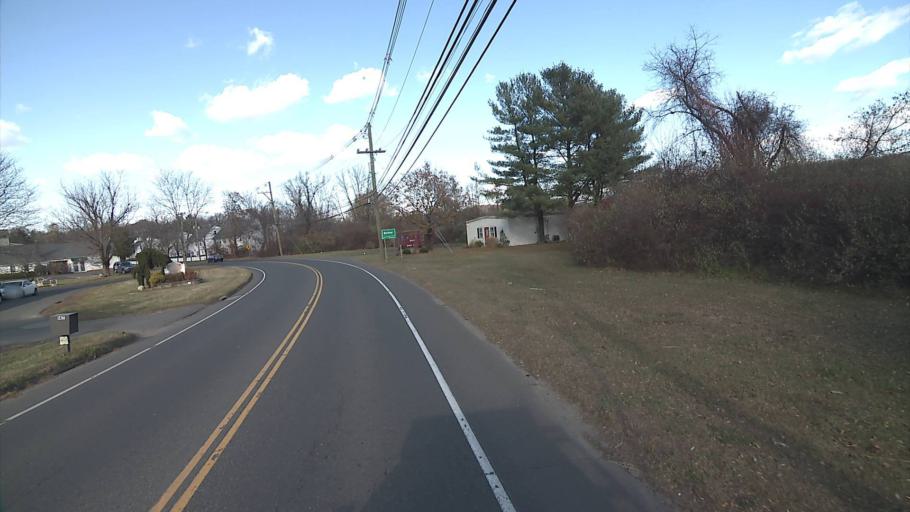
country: US
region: Connecticut
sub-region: Fairfield County
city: Bethel
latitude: 41.3632
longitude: -73.4208
